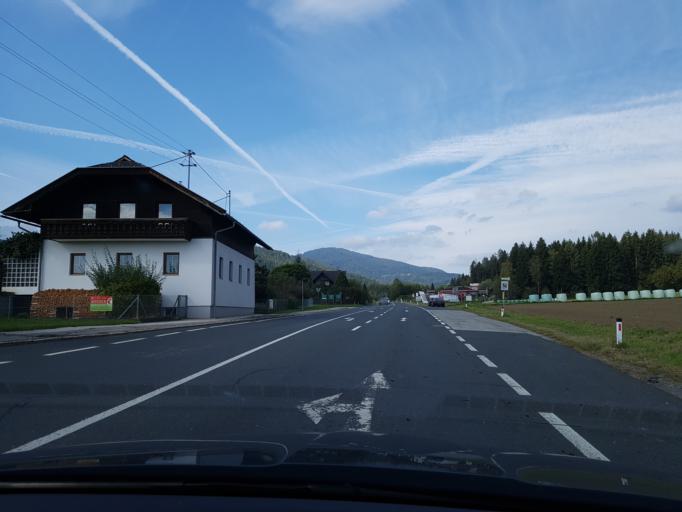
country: AT
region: Carinthia
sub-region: Politischer Bezirk Feldkirchen
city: Himmelberg
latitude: 46.7370
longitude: 14.0604
